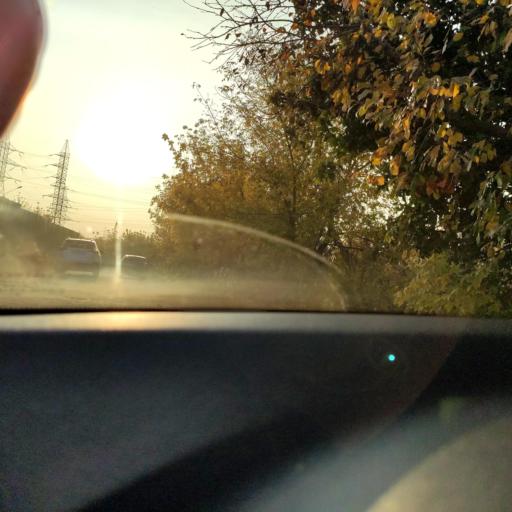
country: RU
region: Samara
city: Petra-Dubrava
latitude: 53.2638
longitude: 50.3017
